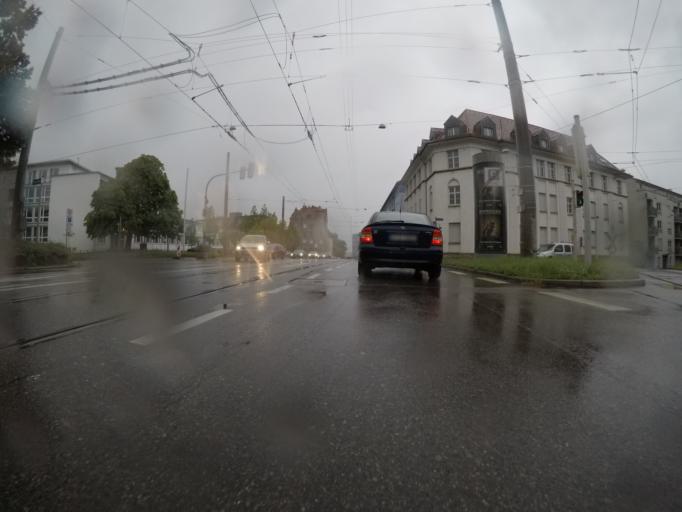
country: DE
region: Baden-Wuerttemberg
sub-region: Regierungsbezirk Stuttgart
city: Stuttgart-Ost
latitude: 48.7889
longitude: 9.2070
